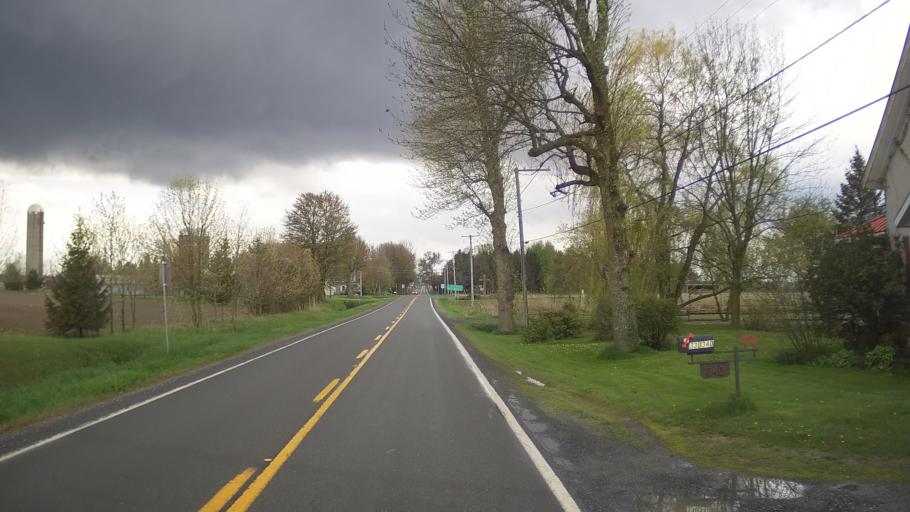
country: CA
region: Quebec
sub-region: Monteregie
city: Farnham
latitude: 45.3046
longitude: -73.1105
